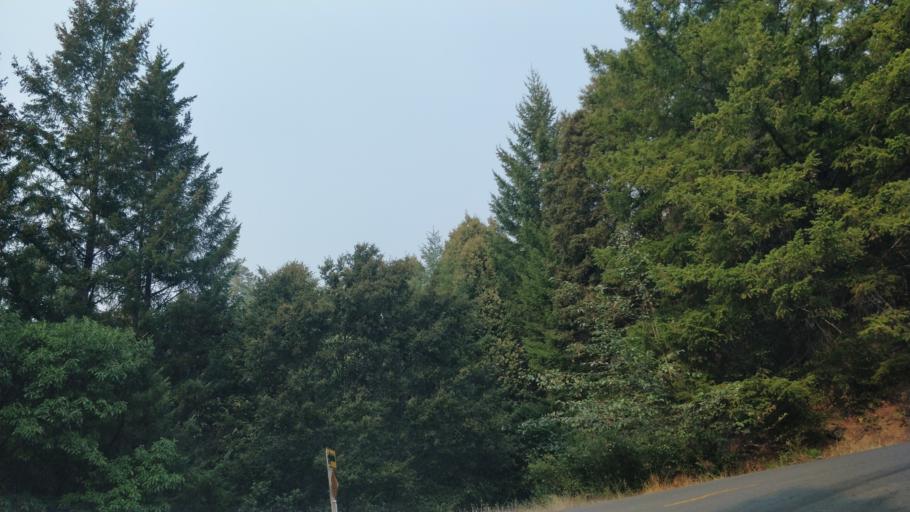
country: US
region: California
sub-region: Humboldt County
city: Rio Dell
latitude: 40.2571
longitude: -124.1203
